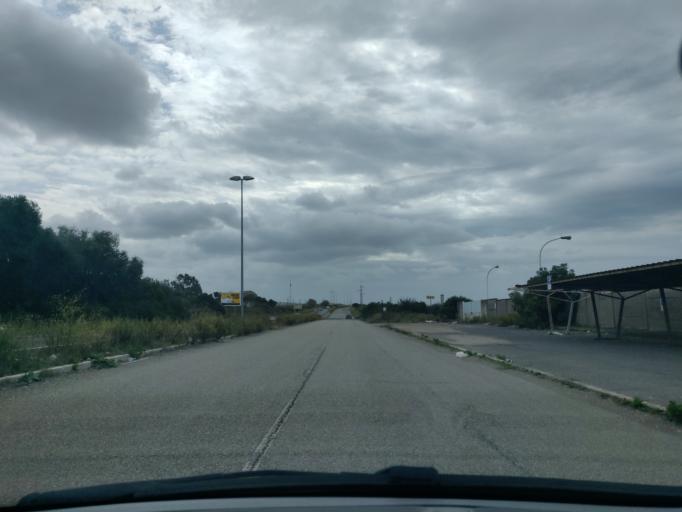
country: IT
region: Latium
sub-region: Citta metropolitana di Roma Capitale
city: Civitavecchia
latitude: 42.1115
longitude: 11.7828
